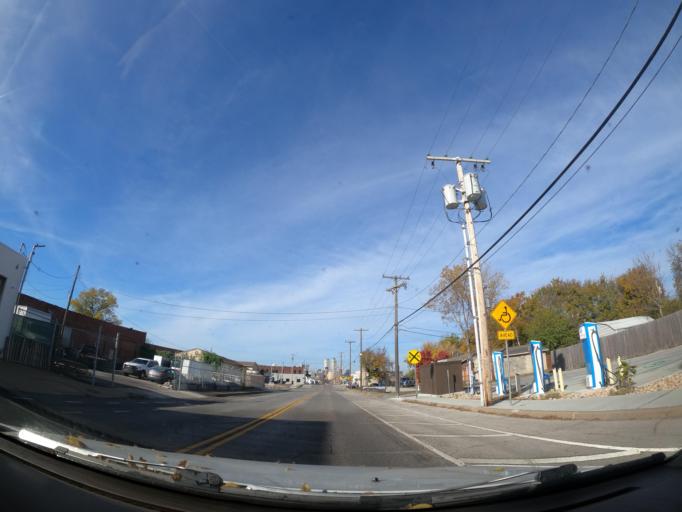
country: US
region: Oklahoma
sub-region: Tulsa County
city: Tulsa
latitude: 36.1521
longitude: -95.9639
